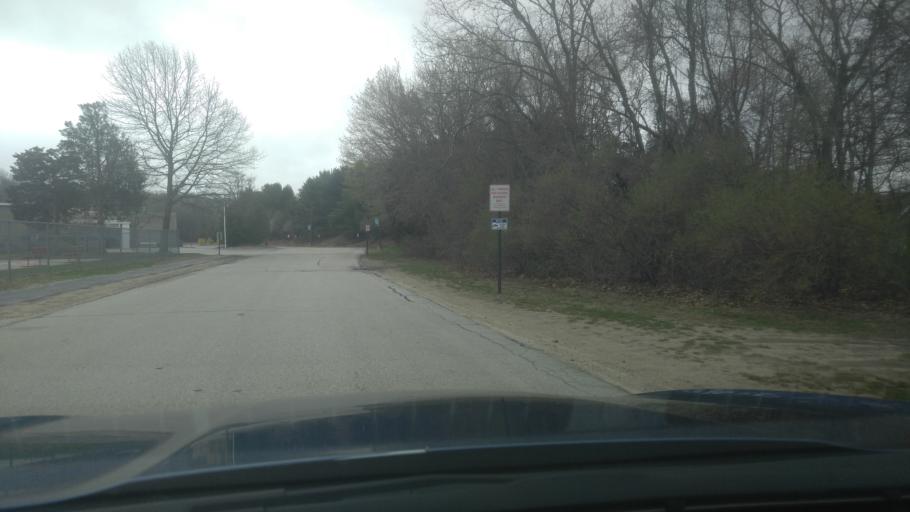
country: US
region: Rhode Island
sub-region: Washington County
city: North Kingstown
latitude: 41.5891
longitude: -71.4451
